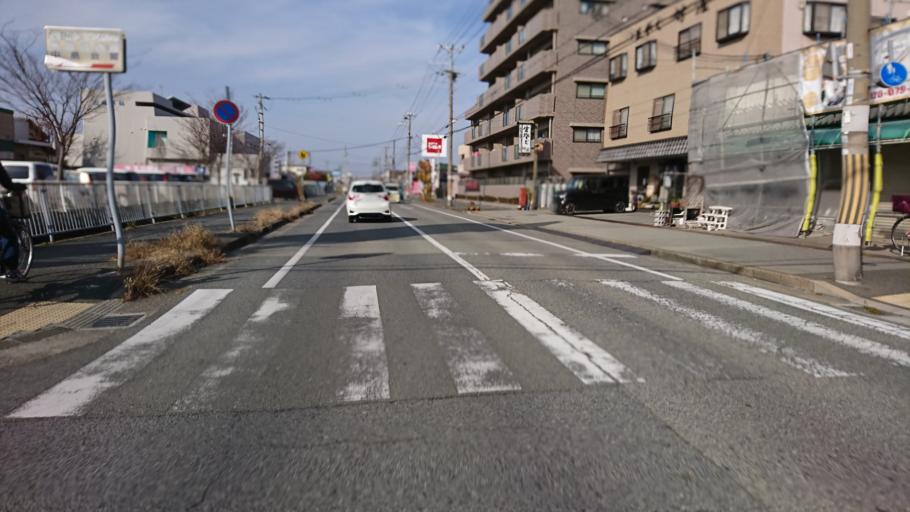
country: JP
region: Hyogo
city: Kakogawacho-honmachi
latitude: 34.7308
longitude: 134.8478
